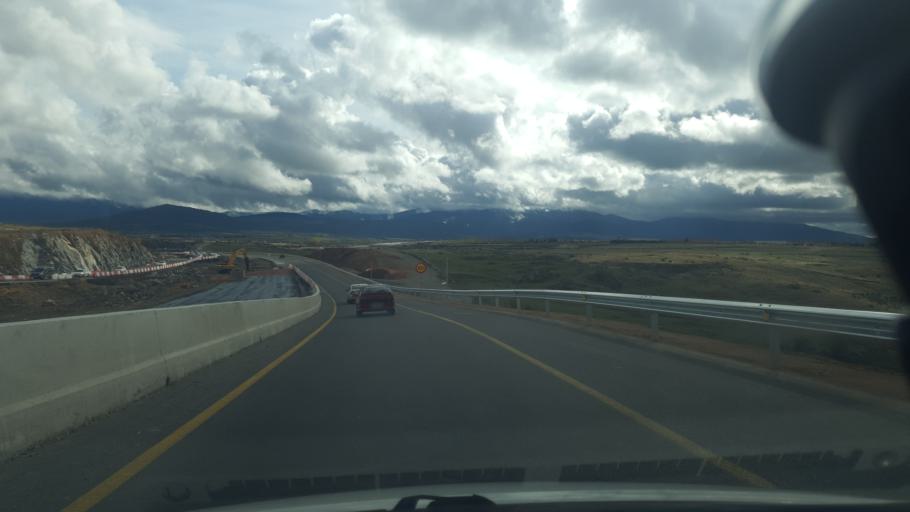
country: ES
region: Castille and Leon
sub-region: Provincia de Segovia
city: San Cristobal de Segovia
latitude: 40.9517
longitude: -4.0909
